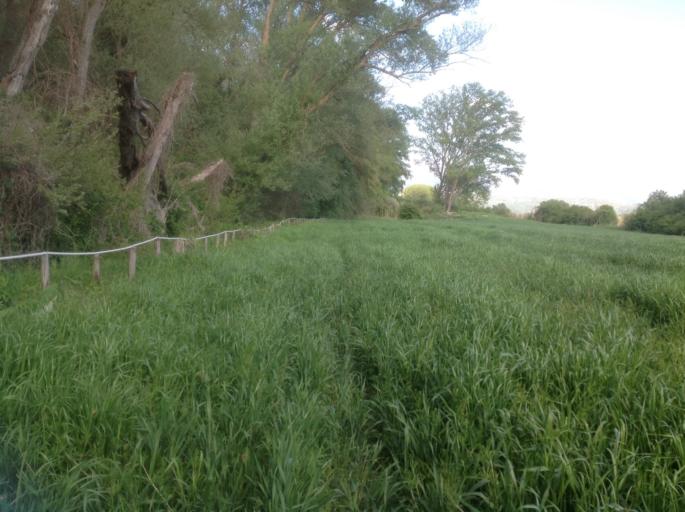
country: IT
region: Latium
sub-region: Provincia di Rieti
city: Colli sul Velino
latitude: 42.4686
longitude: 12.8081
